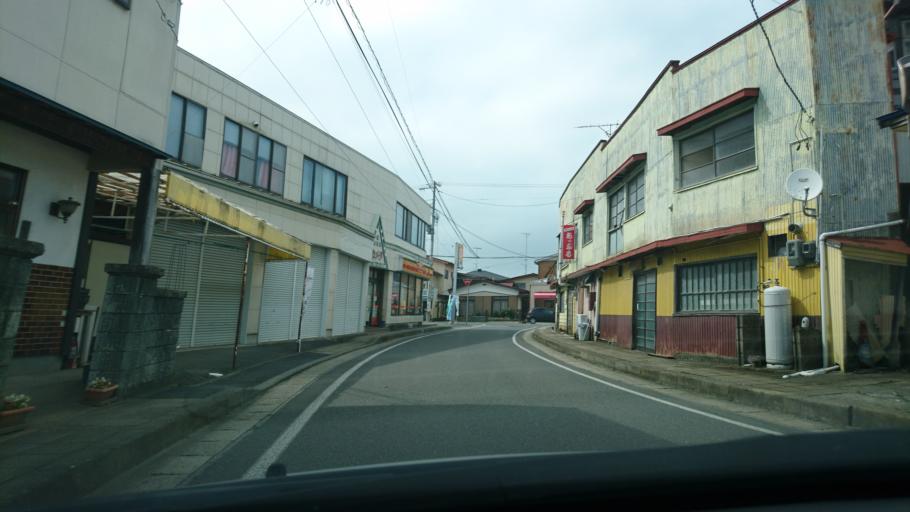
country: JP
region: Iwate
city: Ichinoseki
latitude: 38.8334
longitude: 141.1822
